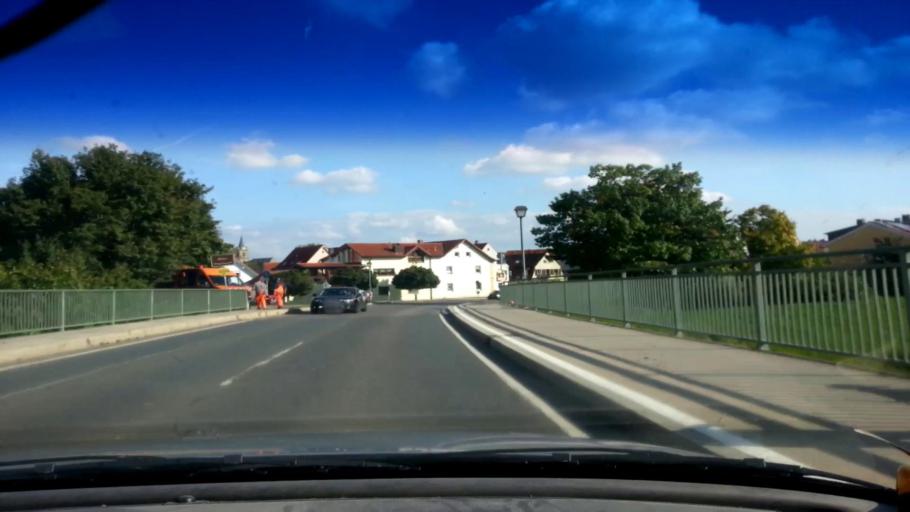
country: DE
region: Bavaria
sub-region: Upper Franconia
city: Hallstadt
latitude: 49.9302
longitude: 10.8682
